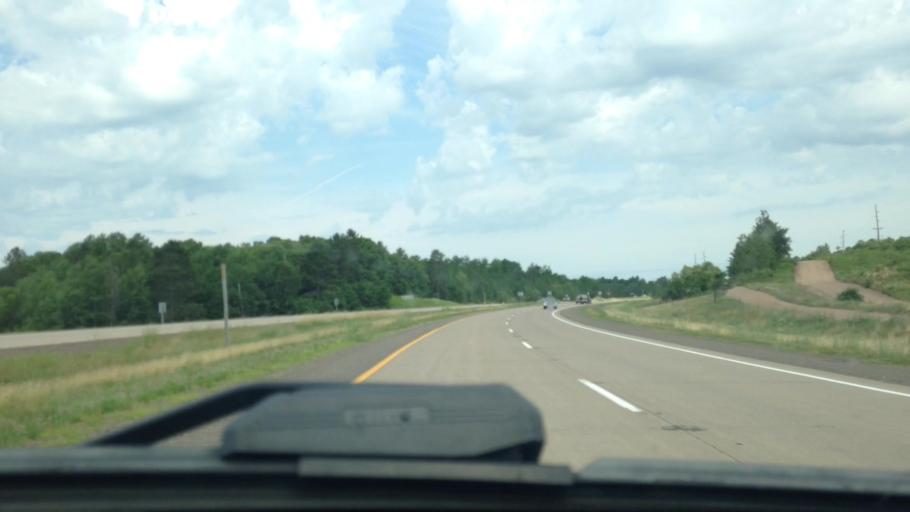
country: US
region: Wisconsin
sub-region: Douglas County
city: Lake Nebagamon
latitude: 46.2184
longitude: -91.7993
